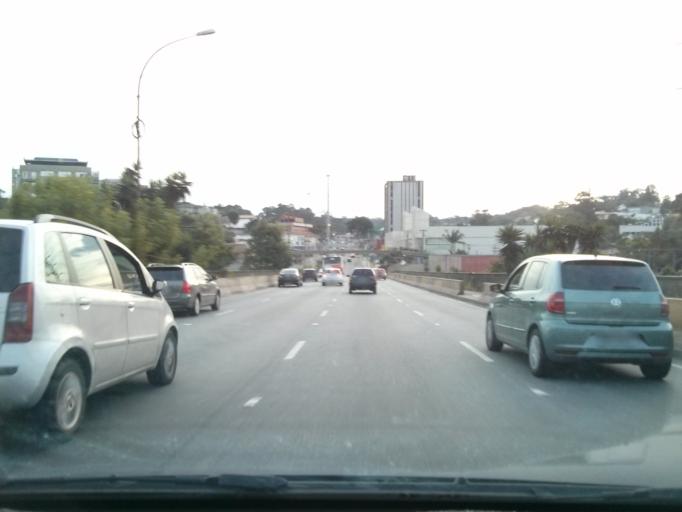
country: BR
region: Sao Paulo
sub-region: Taboao Da Serra
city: Taboao da Serra
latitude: -23.6181
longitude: -46.7010
